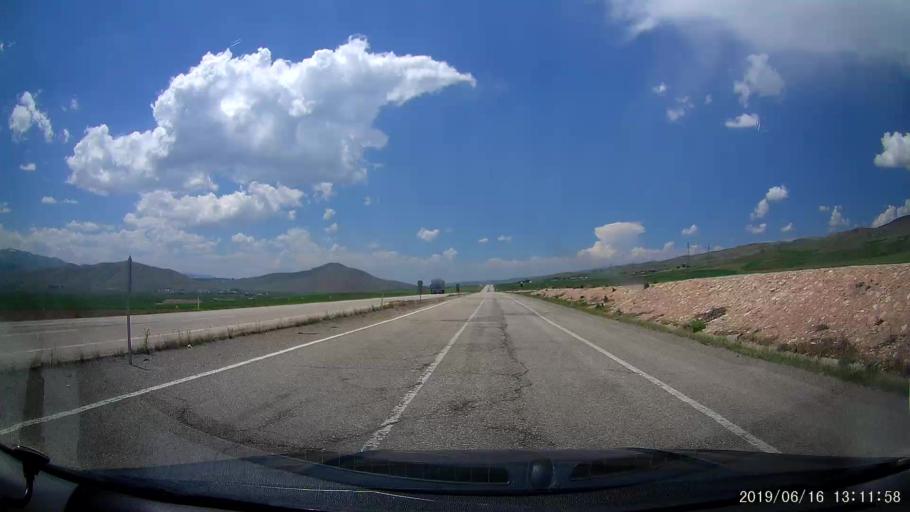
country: TR
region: Agri
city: Diyadin
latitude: 39.5958
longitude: 43.5922
